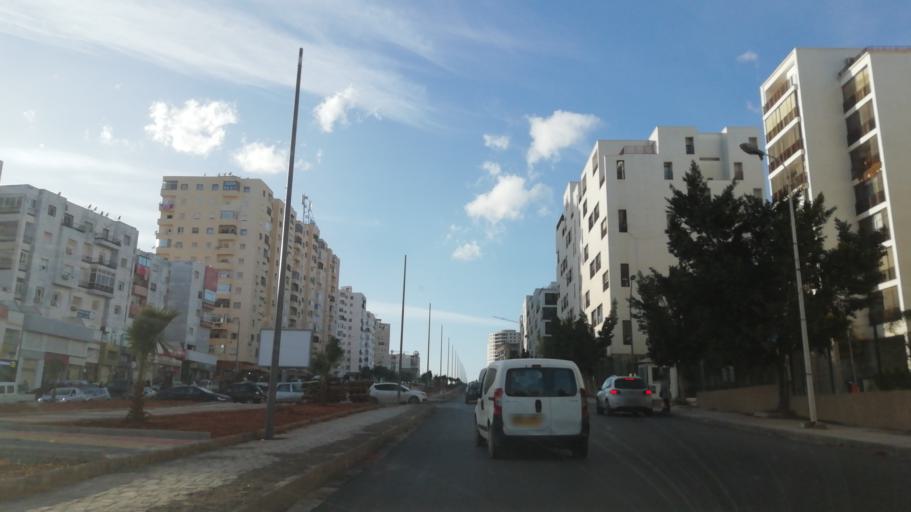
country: DZ
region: Oran
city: Bir el Djir
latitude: 35.7054
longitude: -0.5555
